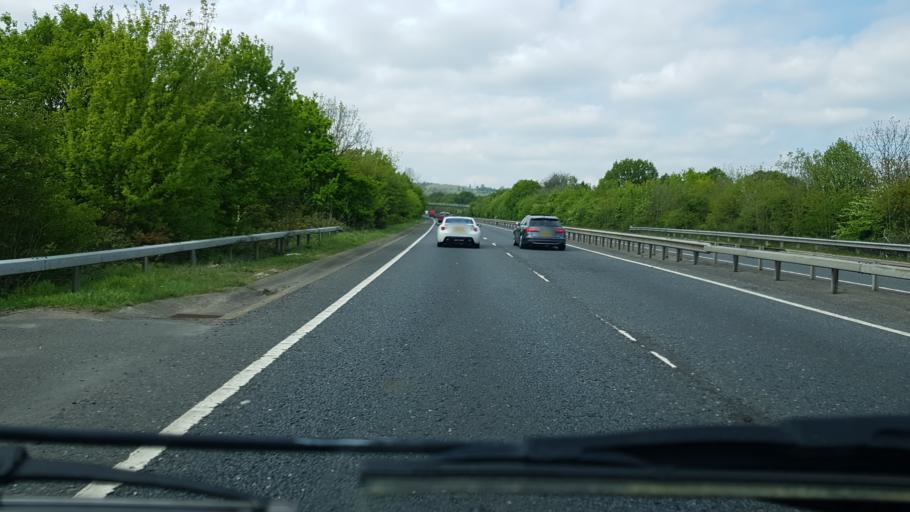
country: GB
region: England
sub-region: Kent
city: Sevenoaks
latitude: 51.2234
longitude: 0.2221
